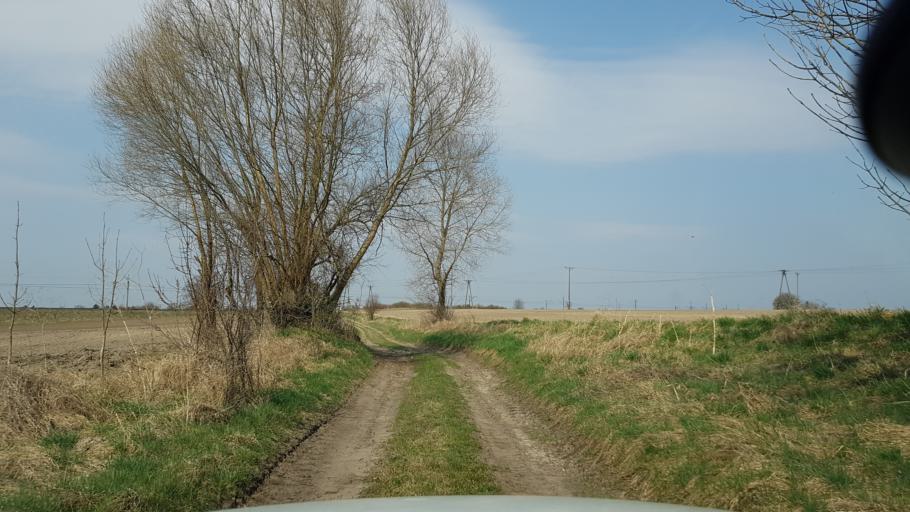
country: PL
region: West Pomeranian Voivodeship
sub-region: Powiat stargardzki
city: Stargard Szczecinski
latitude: 53.3318
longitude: 15.0816
